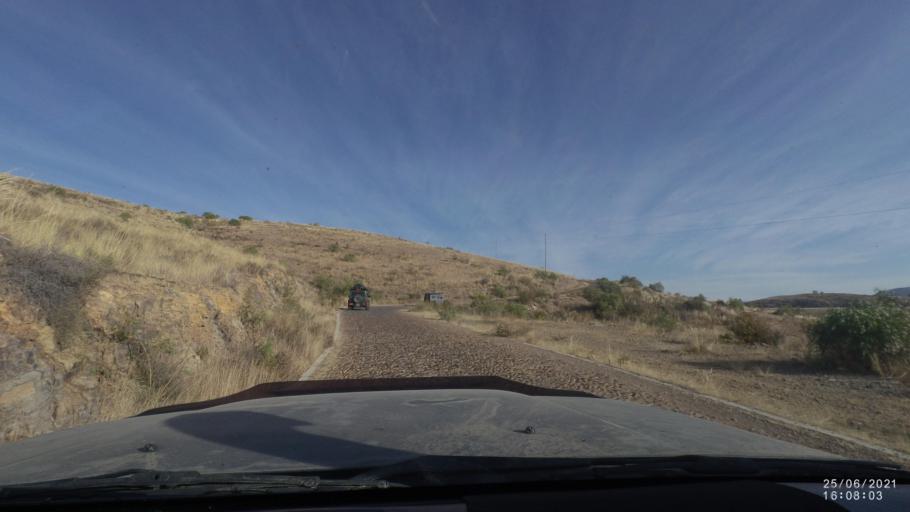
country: BO
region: Cochabamba
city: Cliza
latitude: -17.6805
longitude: -65.9041
